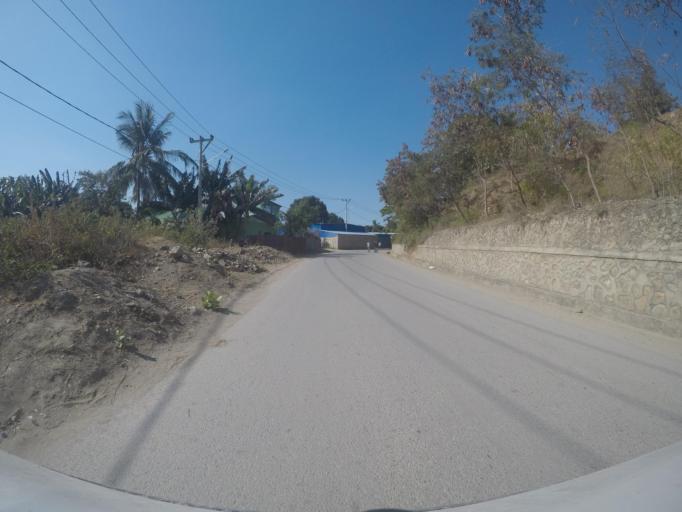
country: TL
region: Dili
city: Dili
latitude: -8.5756
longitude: 125.5372
